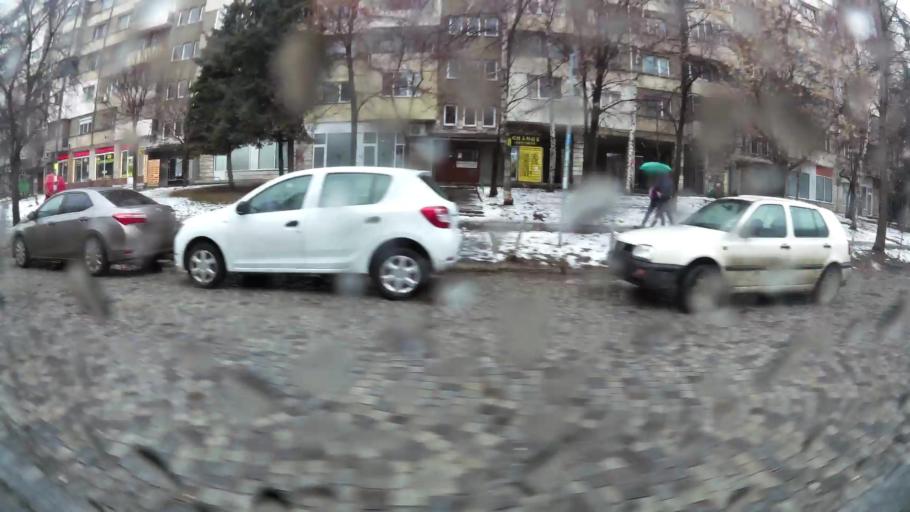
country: BG
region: Sofia-Capital
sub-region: Stolichna Obshtina
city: Sofia
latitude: 42.6742
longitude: 23.2911
